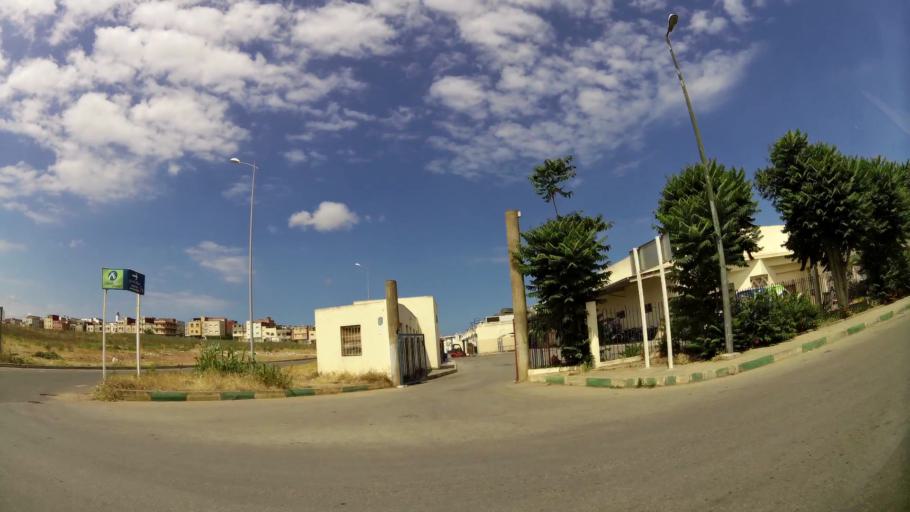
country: MA
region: Gharb-Chrarda-Beni Hssen
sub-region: Kenitra Province
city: Kenitra
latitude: 34.2469
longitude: -6.6078
